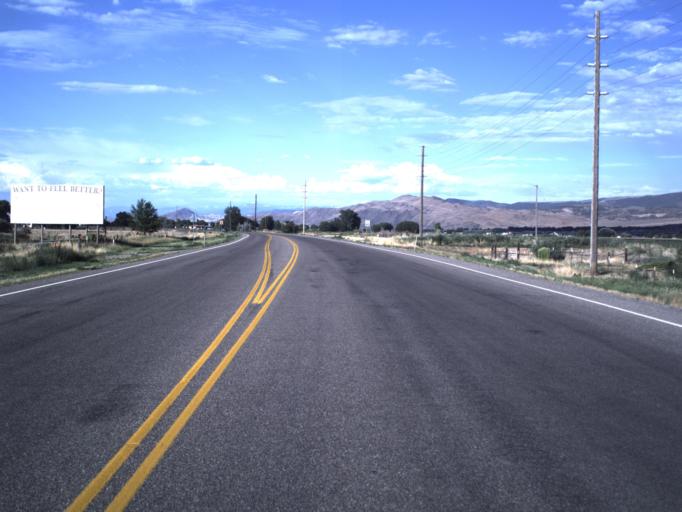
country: US
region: Utah
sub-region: Sevier County
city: Monroe
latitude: 38.6890
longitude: -112.1206
